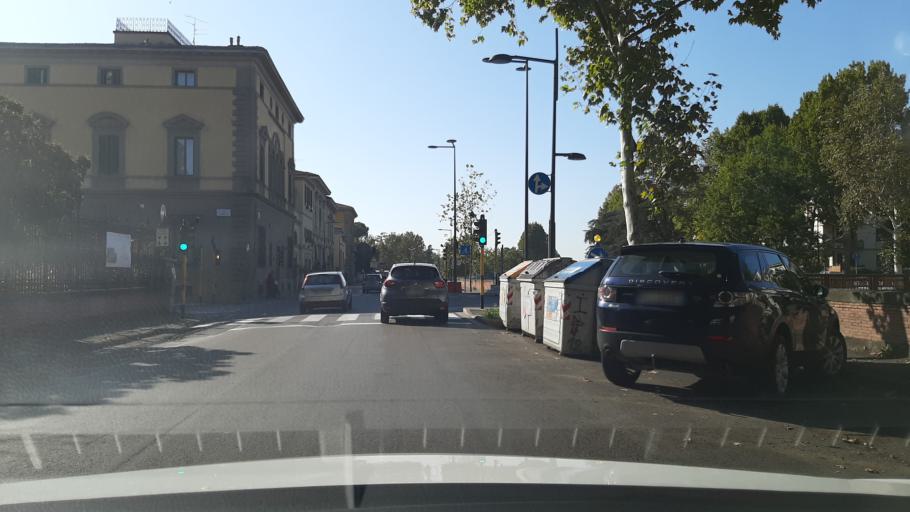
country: IT
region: Tuscany
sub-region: Province of Florence
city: Florence
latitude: 43.7842
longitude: 11.2549
